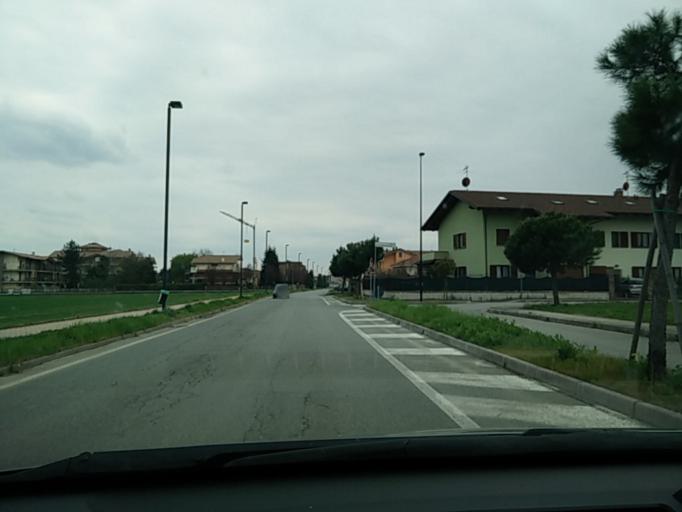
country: IT
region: Piedmont
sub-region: Provincia di Torino
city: Leini
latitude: 45.1937
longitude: 7.7175
